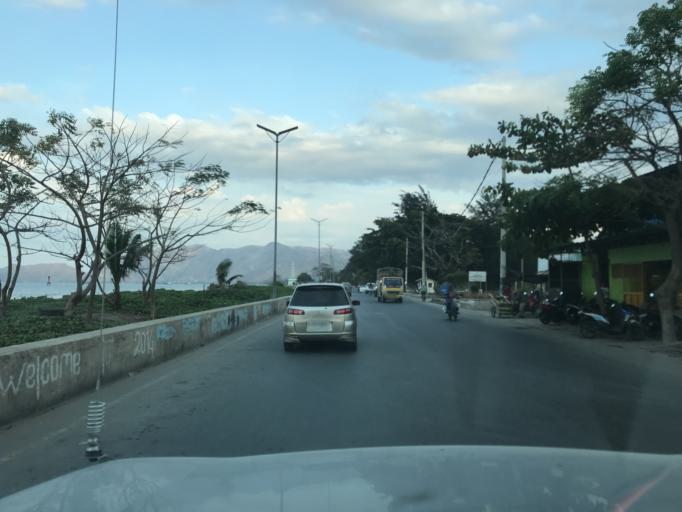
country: TL
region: Dili
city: Dili
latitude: -8.5482
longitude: 125.5642
